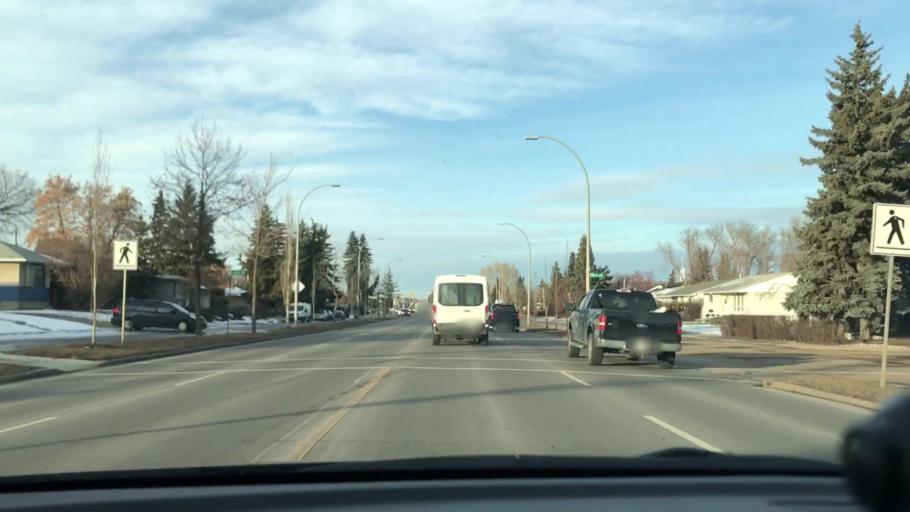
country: CA
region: Alberta
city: Edmonton
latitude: 53.5351
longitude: -113.4430
